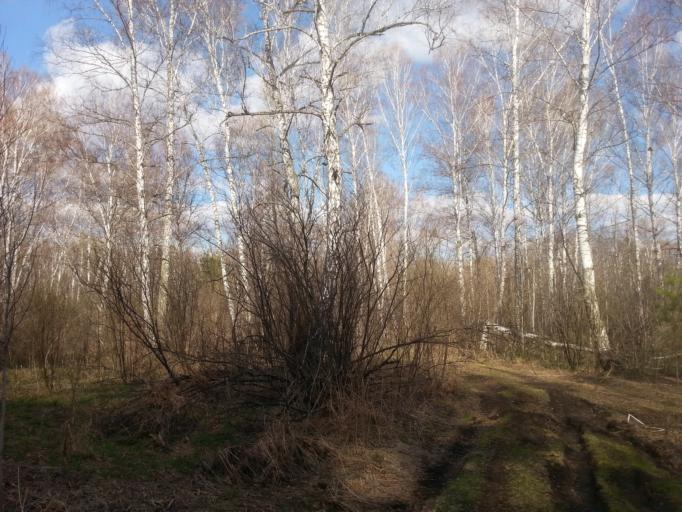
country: RU
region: Altai Krai
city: Sannikovo
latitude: 53.3332
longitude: 84.0112
